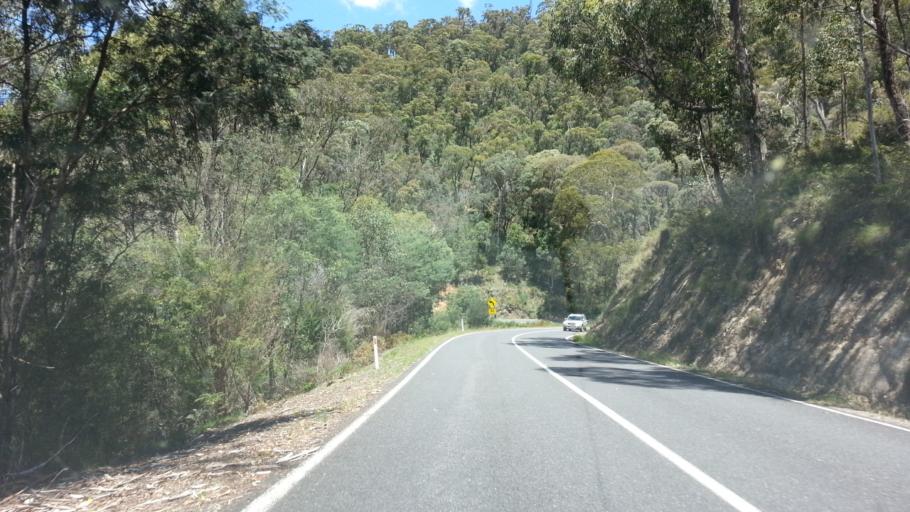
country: AU
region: Victoria
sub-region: Alpine
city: Mount Beauty
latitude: -36.7568
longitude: 147.2030
